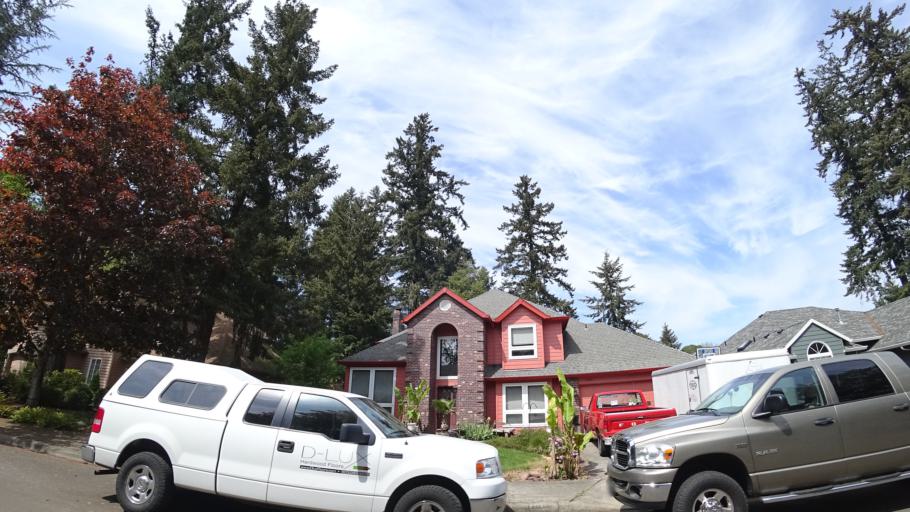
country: US
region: Oregon
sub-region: Washington County
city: Aloha
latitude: 45.4821
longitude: -122.8827
